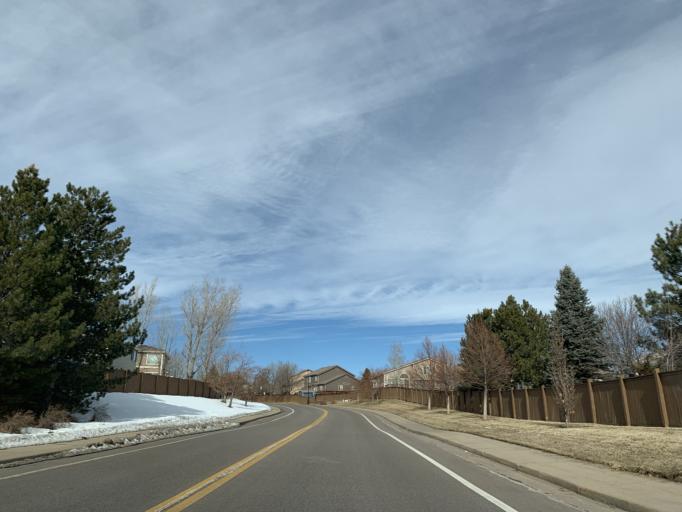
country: US
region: Colorado
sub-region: Douglas County
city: Carriage Club
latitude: 39.5312
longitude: -104.9349
